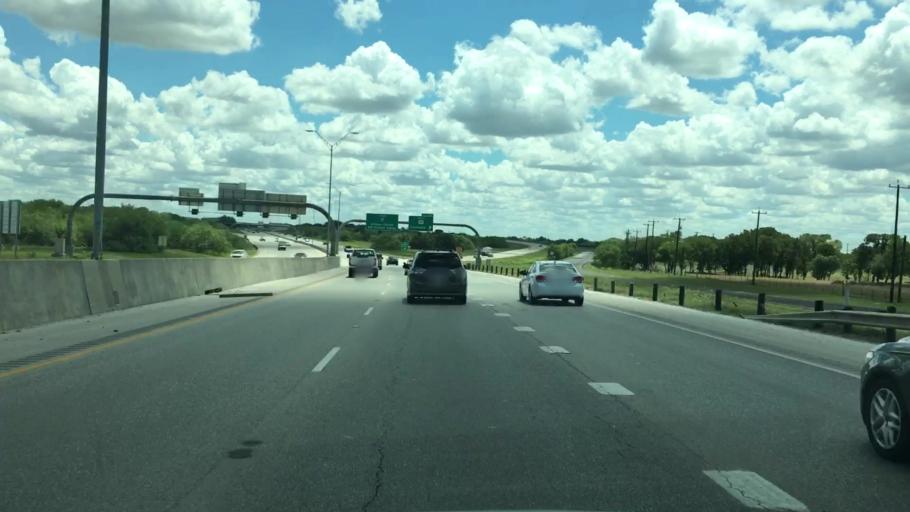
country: US
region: Texas
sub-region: Bexar County
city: Elmendorf
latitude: 29.3142
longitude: -98.4056
